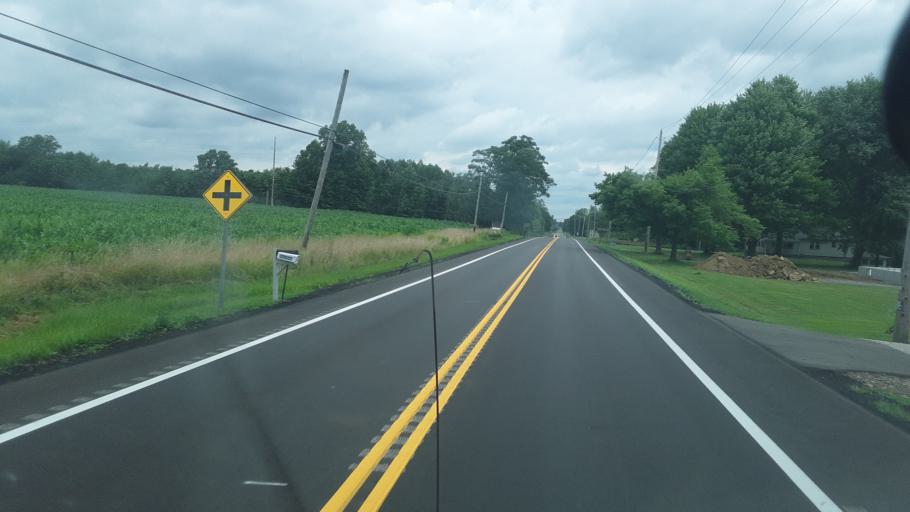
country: US
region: Ohio
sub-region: Trumbull County
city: Howland Center
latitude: 41.2702
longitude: -80.6632
